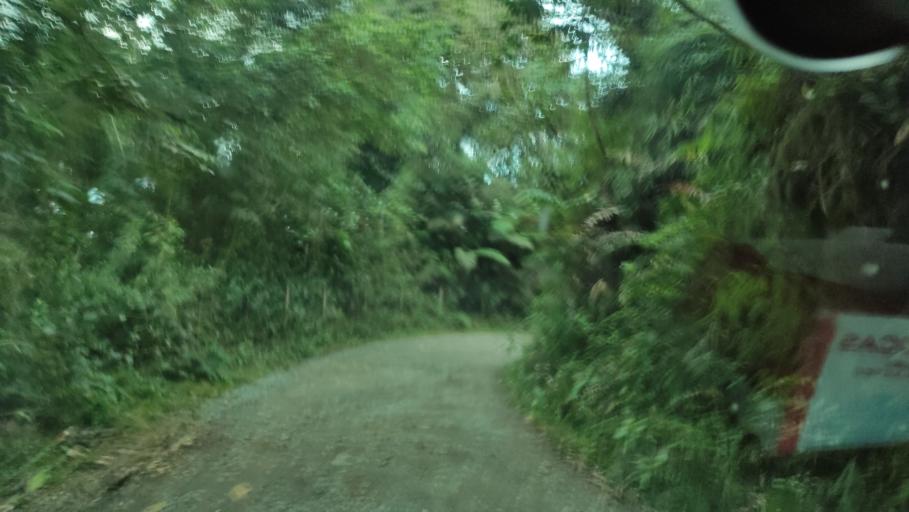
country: CO
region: Valle del Cauca
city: San Pedro
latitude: 3.8783
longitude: -76.1452
